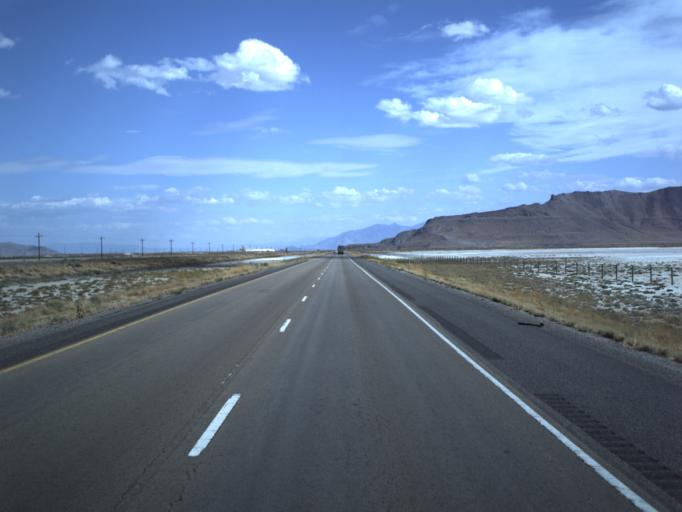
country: US
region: Utah
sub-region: Tooele County
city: Grantsville
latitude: 40.7515
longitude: -112.7121
